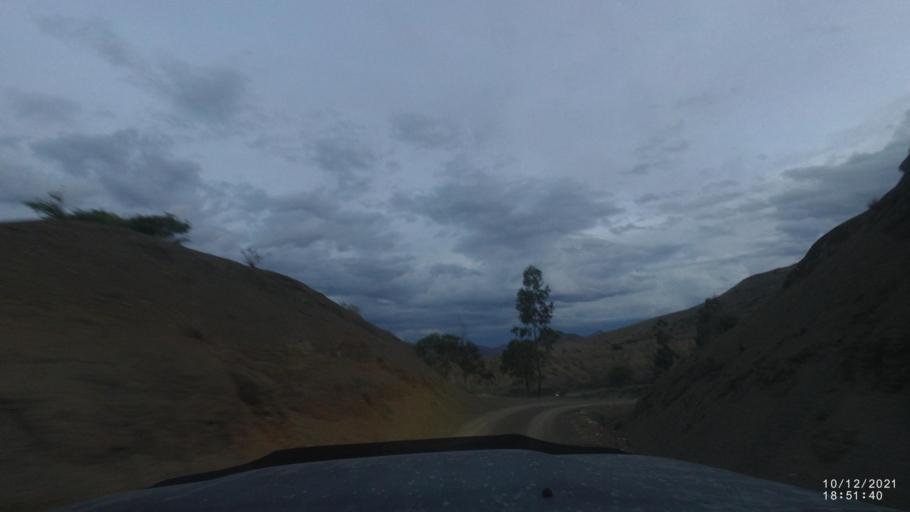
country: BO
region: Cochabamba
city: Tarata
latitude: -17.8824
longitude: -65.9649
